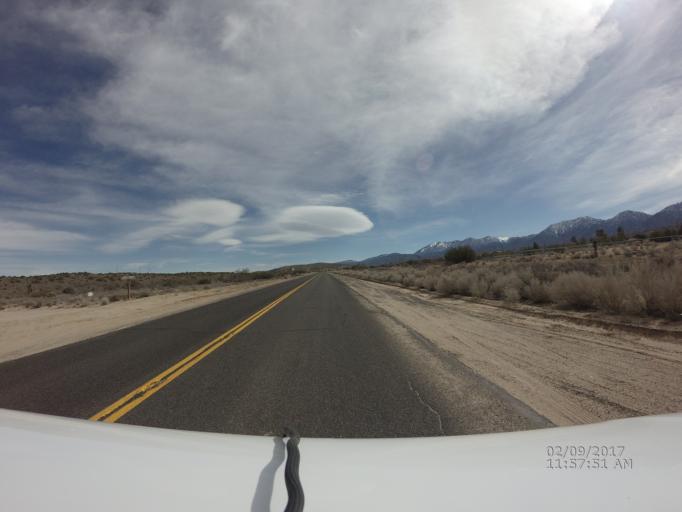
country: US
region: California
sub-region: Los Angeles County
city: Littlerock
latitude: 34.4795
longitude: -117.9113
